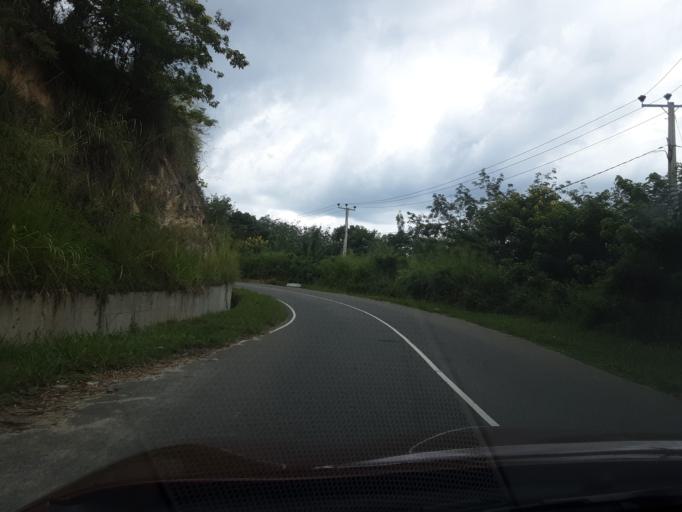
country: LK
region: Uva
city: Monaragala
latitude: 6.9074
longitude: 81.2092
